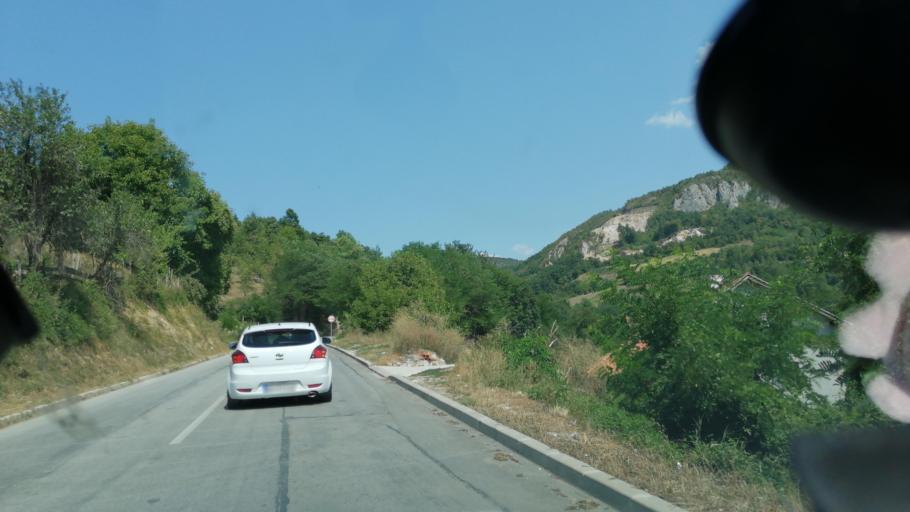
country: RS
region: Central Serbia
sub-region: Moravicki Okrug
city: Ivanjica
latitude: 43.6186
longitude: 20.2373
